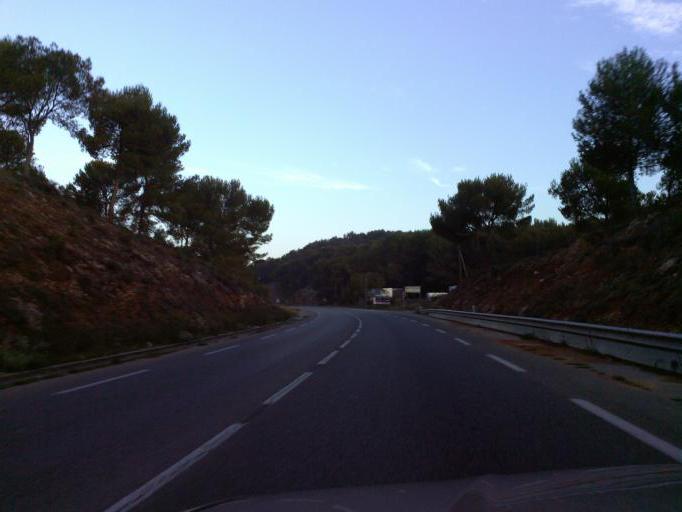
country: FR
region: Provence-Alpes-Cote d'Azur
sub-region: Departement des Bouches-du-Rhone
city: Lambesc
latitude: 43.6440
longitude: 5.2782
